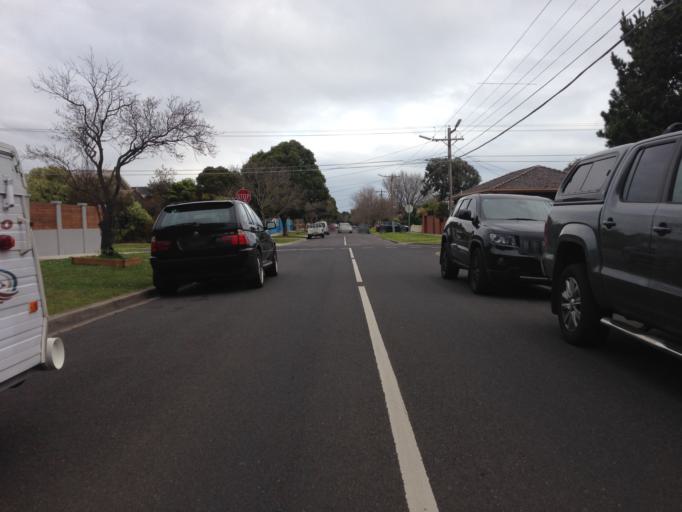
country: AU
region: Victoria
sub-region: Darebin
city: Preston
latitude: -37.7609
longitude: 145.0167
